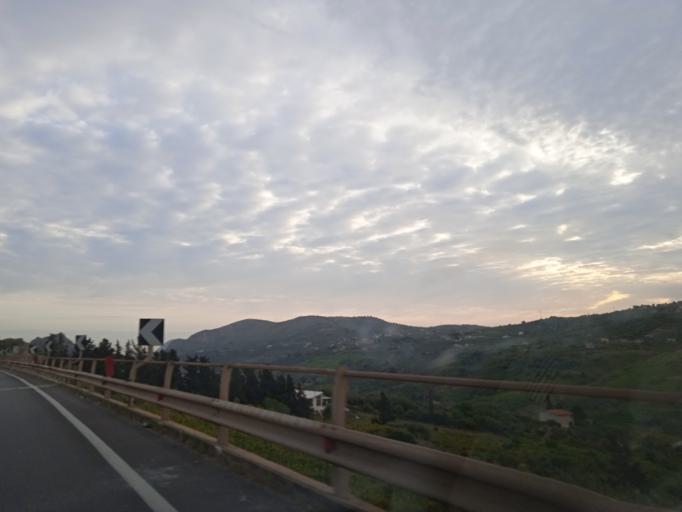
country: IT
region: Sicily
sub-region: Palermo
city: Portella di Mare
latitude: 38.0492
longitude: 13.4612
